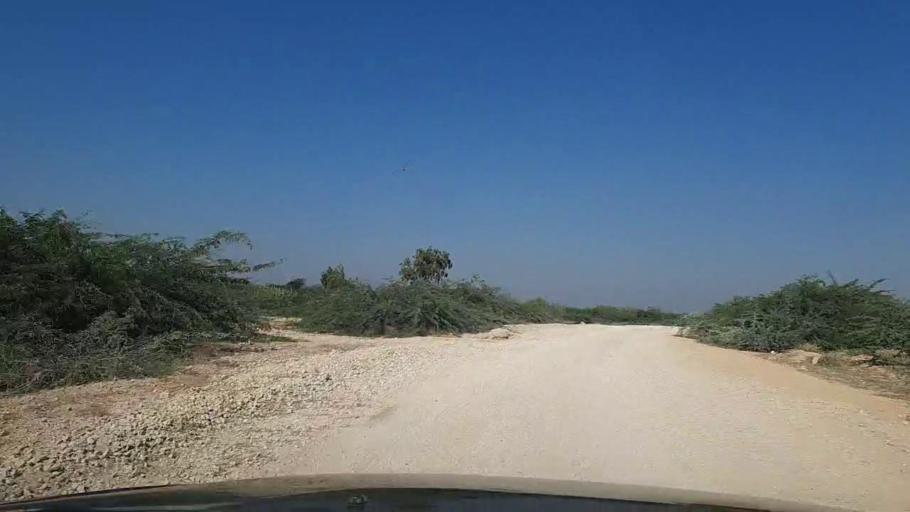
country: PK
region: Sindh
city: Thatta
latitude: 24.6247
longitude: 67.8351
